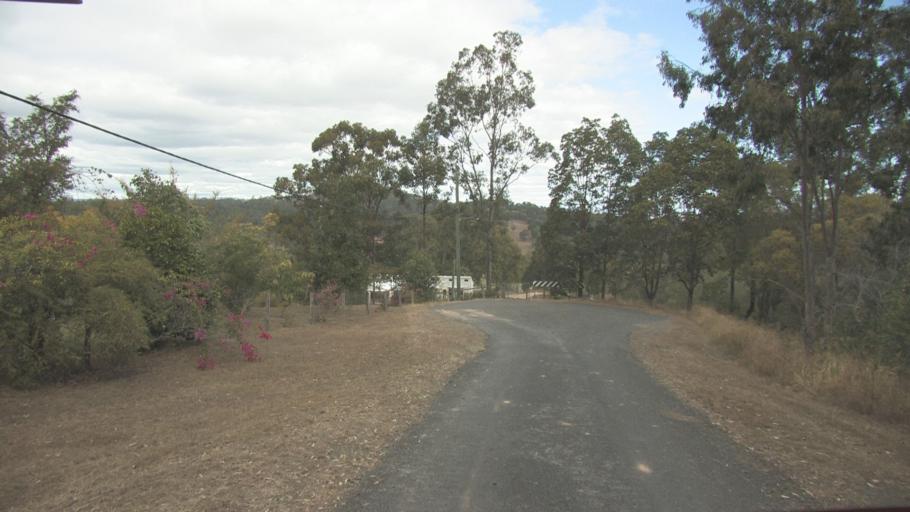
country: AU
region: Queensland
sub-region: Logan
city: Cedar Vale
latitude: -27.9024
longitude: 153.0388
